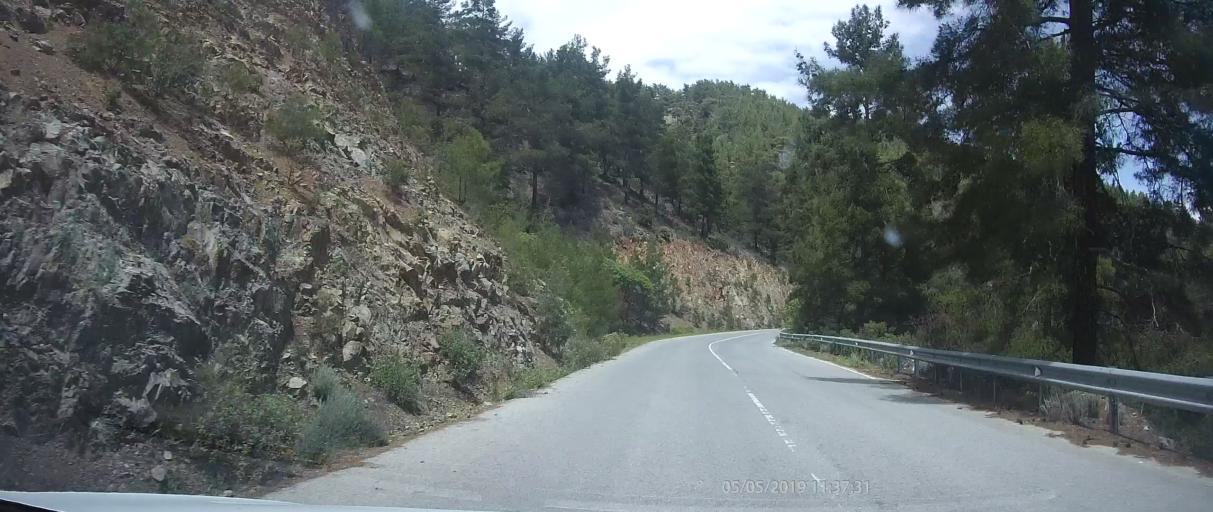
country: CY
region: Lefkosia
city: Kato Pyrgos
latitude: 34.9738
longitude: 32.6587
